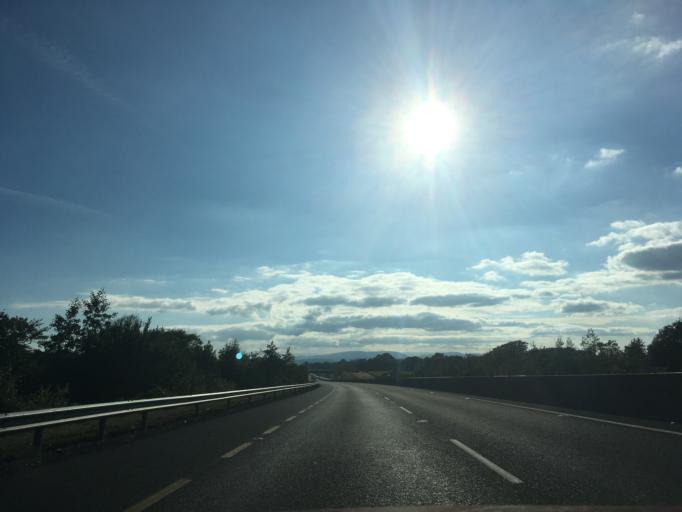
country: IE
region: Munster
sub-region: Waterford
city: Waterford
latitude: 52.2900
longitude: -7.1140
